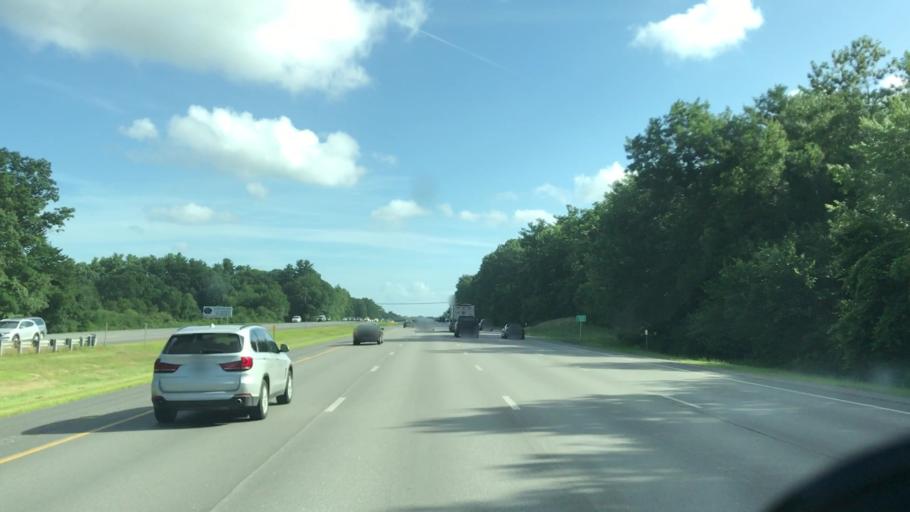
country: US
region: New Hampshire
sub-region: Rockingham County
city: Seabrook
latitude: 42.9039
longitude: -70.8780
